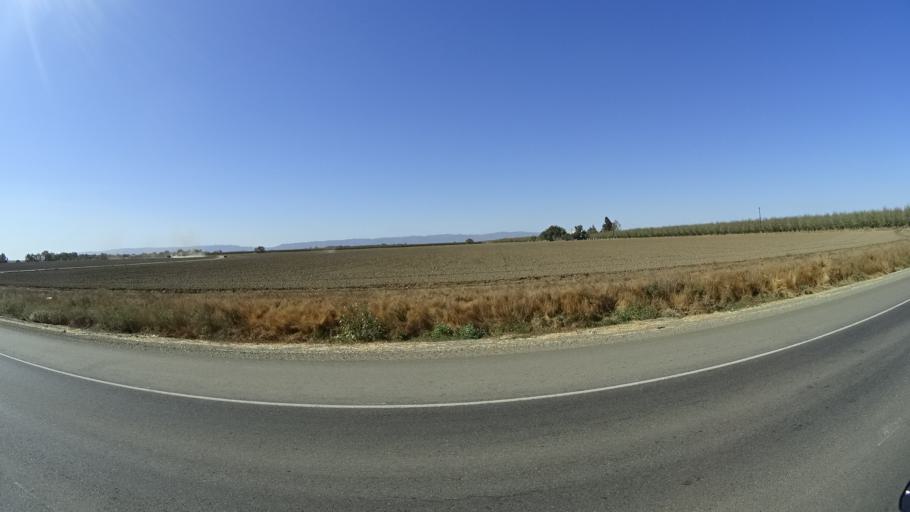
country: US
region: California
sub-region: Yolo County
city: Davis
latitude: 38.5965
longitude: -121.8028
